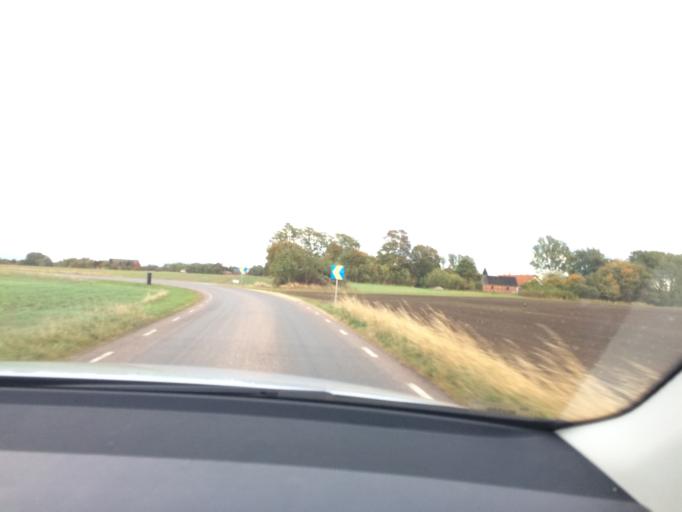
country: SE
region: Skane
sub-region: Hoors Kommun
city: Loberod
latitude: 55.7841
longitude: 13.4387
